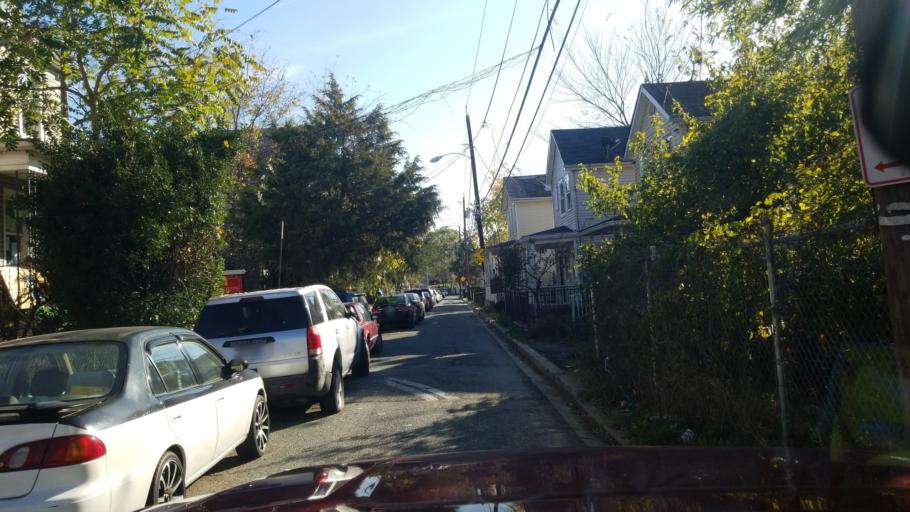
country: US
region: Maryland
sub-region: Prince George's County
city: Fairmount Heights
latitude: 38.8992
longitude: -76.9250
